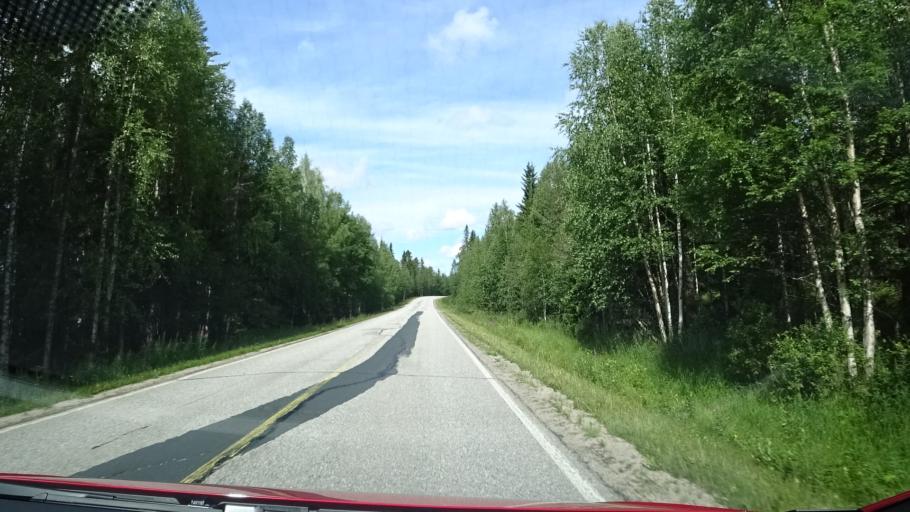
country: FI
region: Kainuu
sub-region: Kehys-Kainuu
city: Kuhmo
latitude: 64.4525
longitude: 29.7774
